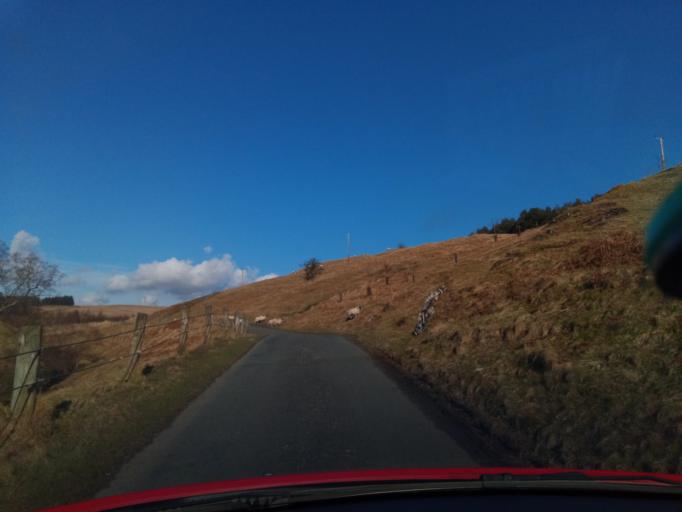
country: GB
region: Scotland
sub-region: The Scottish Borders
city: Hawick
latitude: 55.4267
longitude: -2.8748
